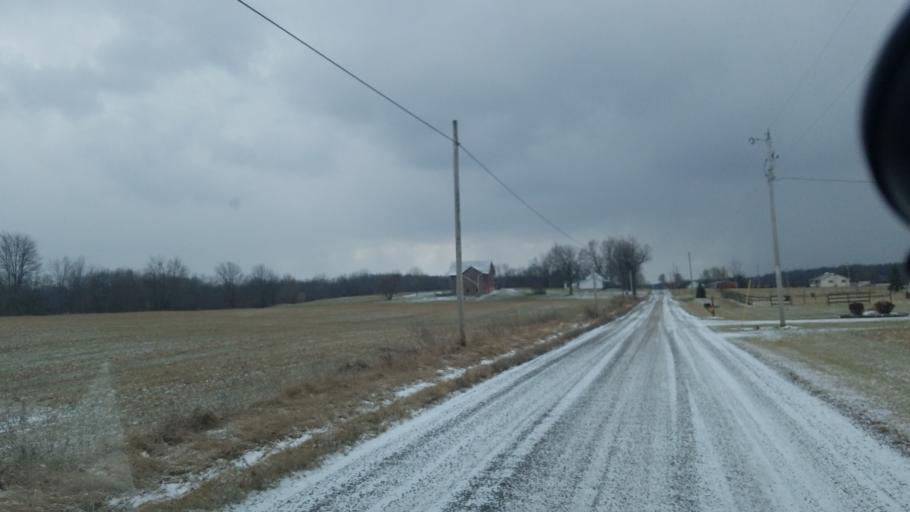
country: US
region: Ohio
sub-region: Morrow County
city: Mount Gilead
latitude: 40.5917
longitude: -82.7908
